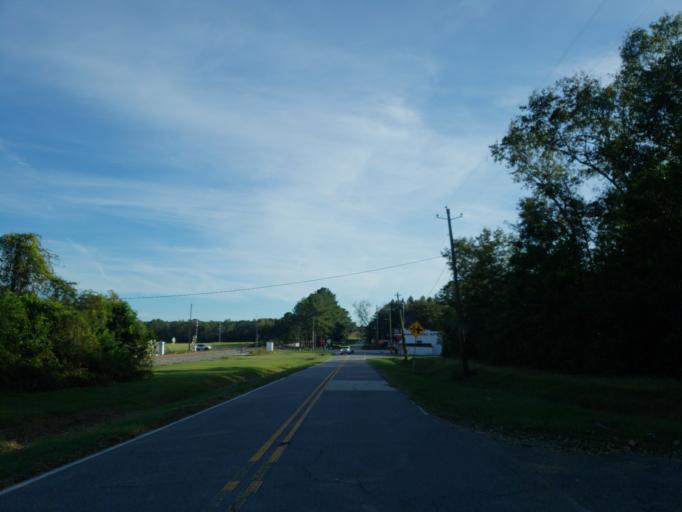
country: US
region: Georgia
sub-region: Dooly County
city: Vienna
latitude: 32.0920
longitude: -83.7876
